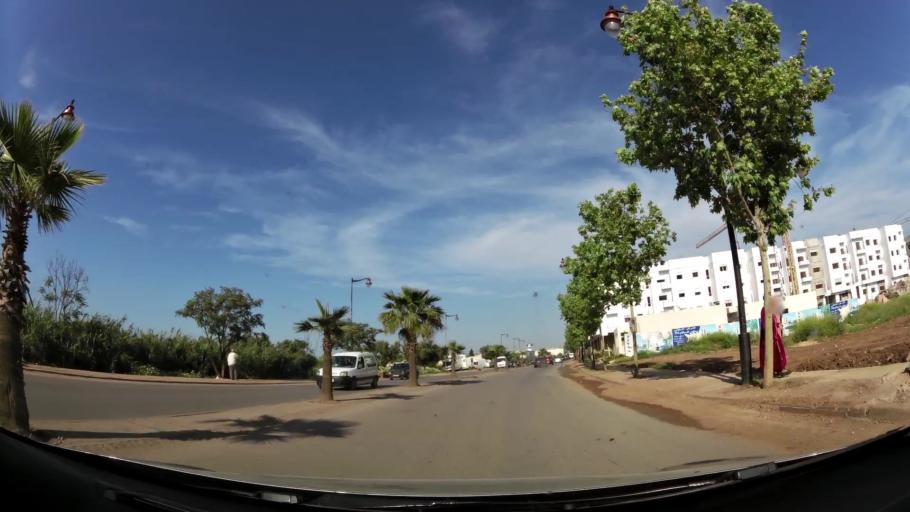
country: MA
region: Fes-Boulemane
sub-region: Fes
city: Fes
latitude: 34.0269
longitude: -5.0303
